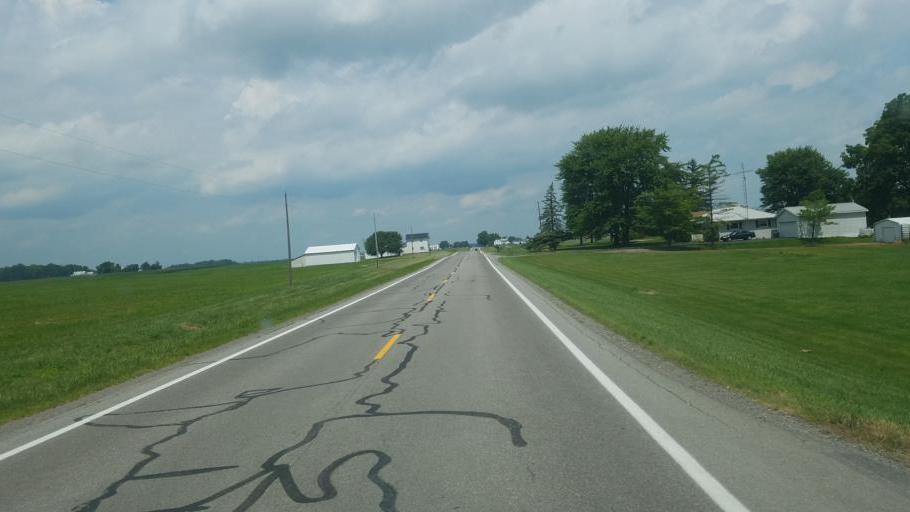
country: US
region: Ohio
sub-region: Hardin County
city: Kenton
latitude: 40.5879
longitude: -83.5926
